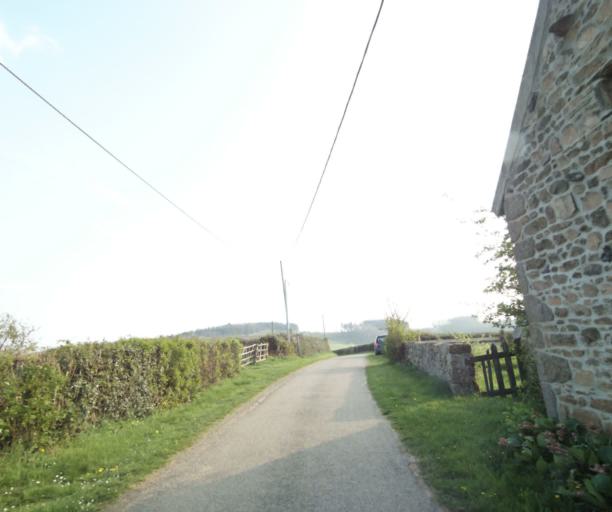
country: FR
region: Bourgogne
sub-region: Departement de Saone-et-Loire
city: Matour
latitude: 46.4257
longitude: 4.4820
